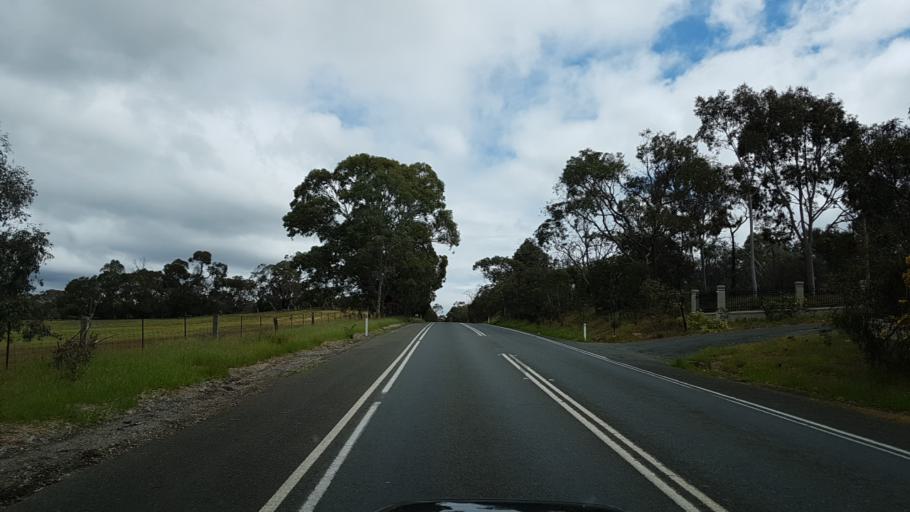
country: AU
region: South Australia
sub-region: Playford
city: One Tree Hill
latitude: -34.7176
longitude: 138.7778
